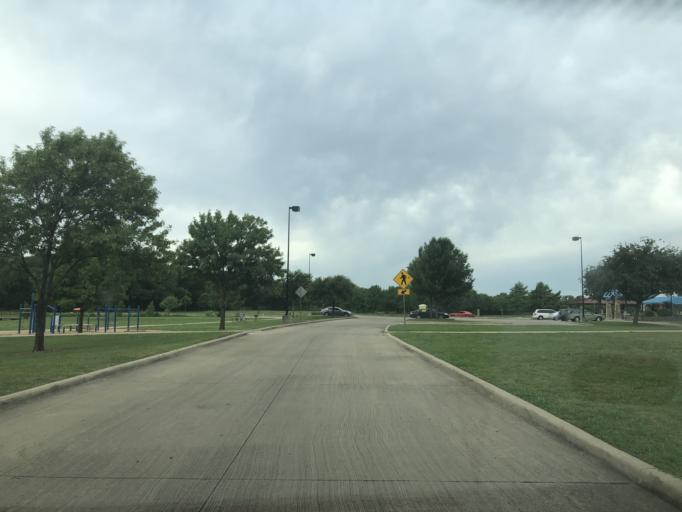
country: US
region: Texas
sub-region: Dallas County
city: Irving
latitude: 32.7867
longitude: -96.9783
